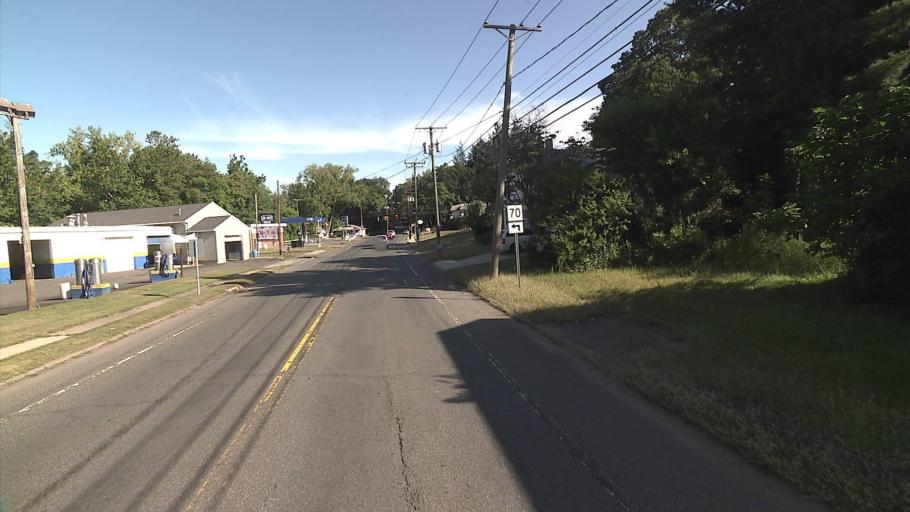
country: US
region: Connecticut
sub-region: New Haven County
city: Meriden
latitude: 41.5169
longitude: -72.8253
